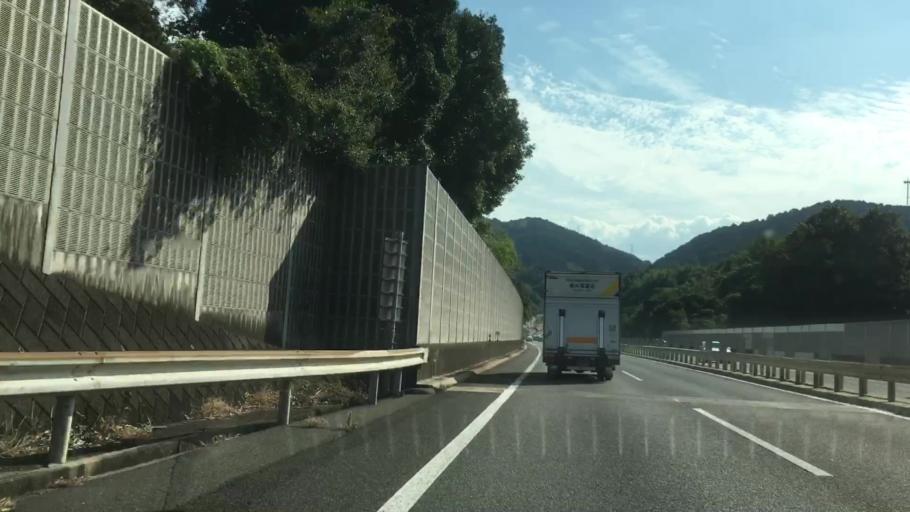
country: JP
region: Yamaguchi
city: Otake
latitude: 34.2403
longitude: 132.2150
